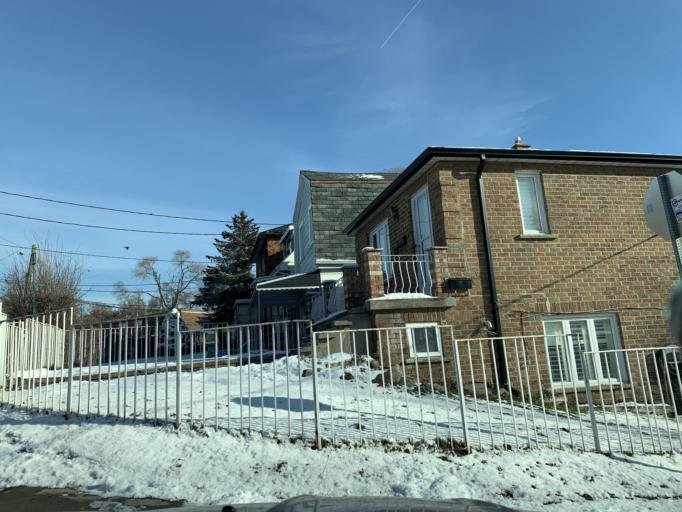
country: CA
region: Ontario
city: Toronto
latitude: 43.6805
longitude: -79.4849
